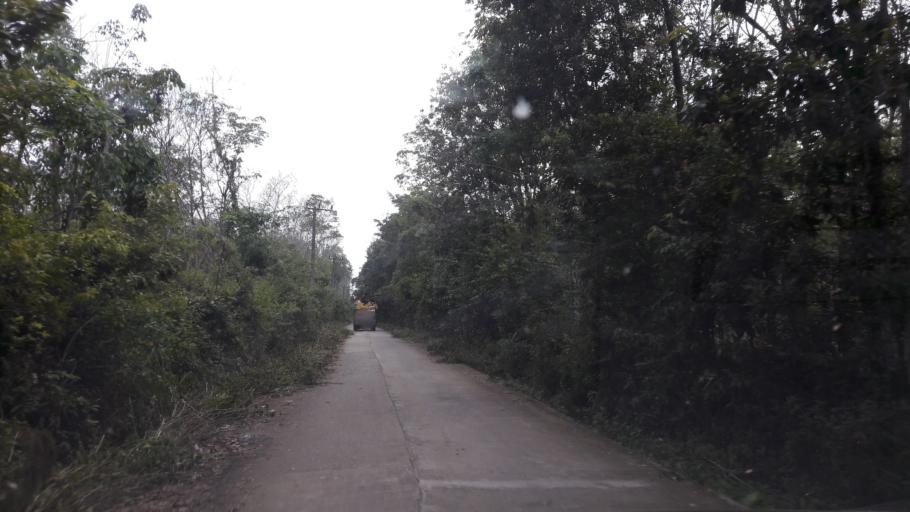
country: ID
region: South Sumatra
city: Gunungmenang
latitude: -3.1028
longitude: 104.0705
